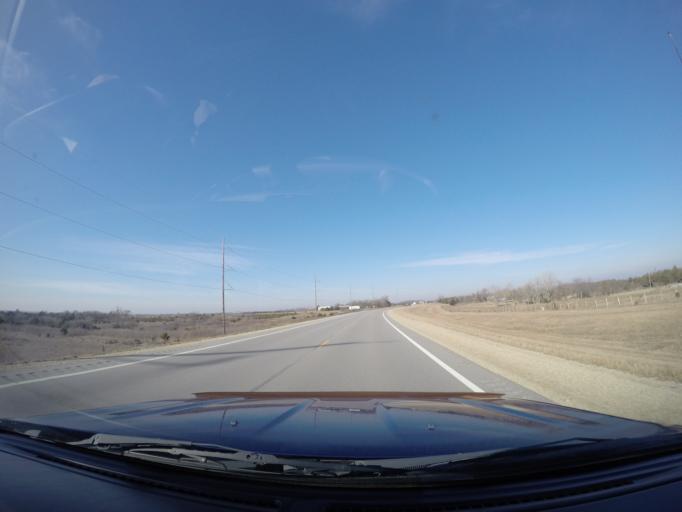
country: US
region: Kansas
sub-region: Riley County
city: Manhattan
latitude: 39.2524
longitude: -96.6679
